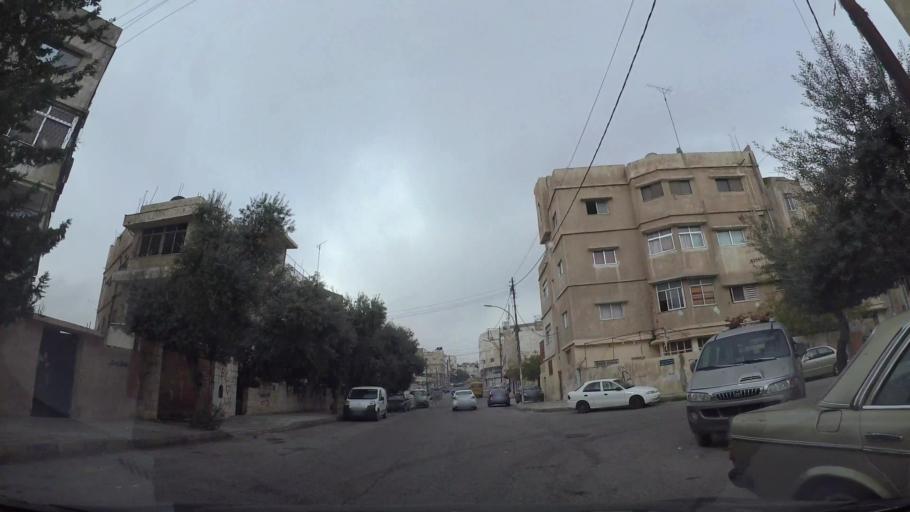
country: JO
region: Amman
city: Amman
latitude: 31.9693
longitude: 35.9324
